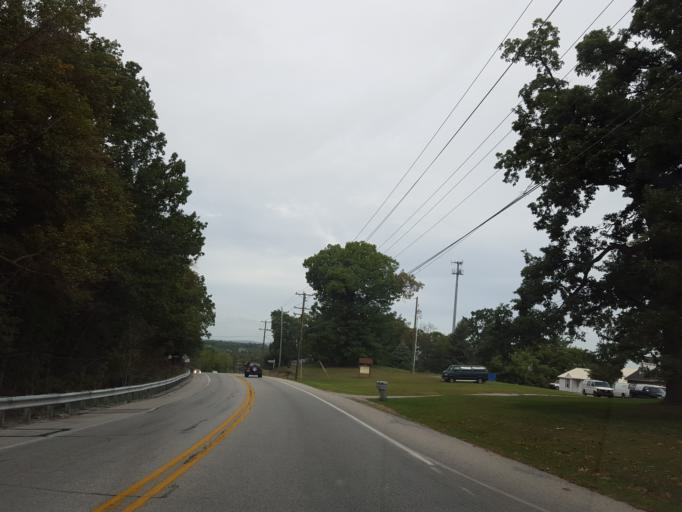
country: US
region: Pennsylvania
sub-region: York County
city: West York
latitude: 39.9126
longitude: -76.7923
